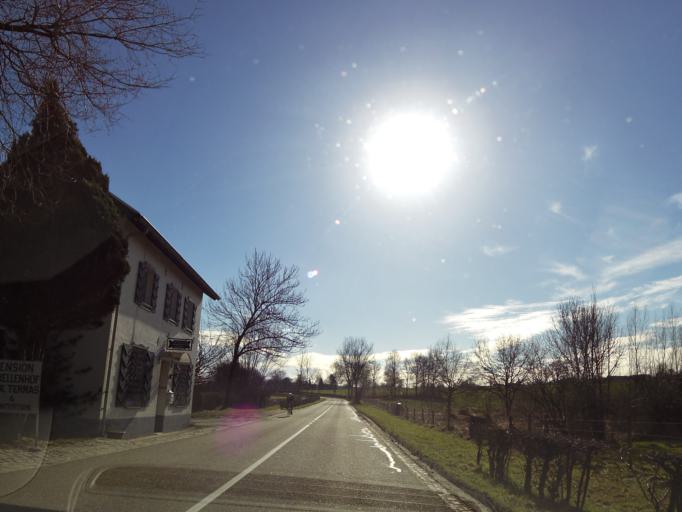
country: BE
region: Wallonia
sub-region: Province de Liege
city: Plombieres
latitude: 50.7842
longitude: 5.9189
